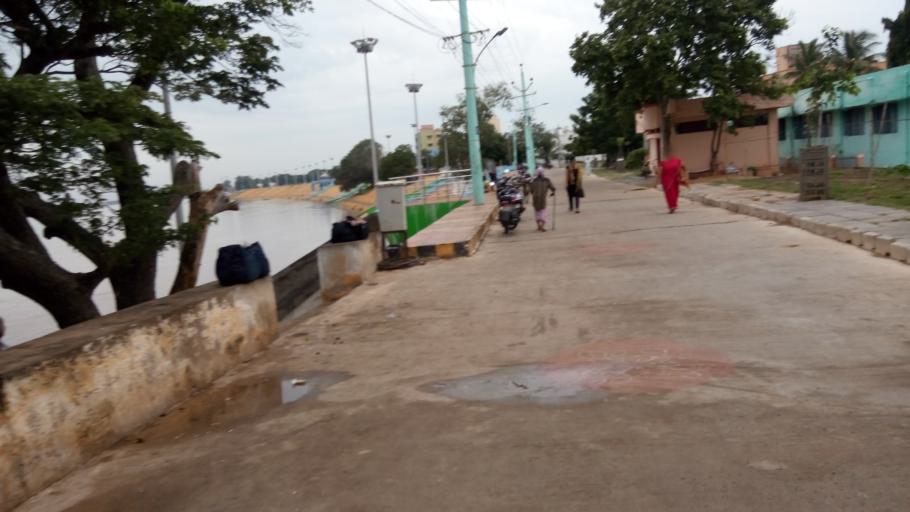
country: IN
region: Andhra Pradesh
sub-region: East Godavari
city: Rajahmundry
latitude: 17.0136
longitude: 81.7699
